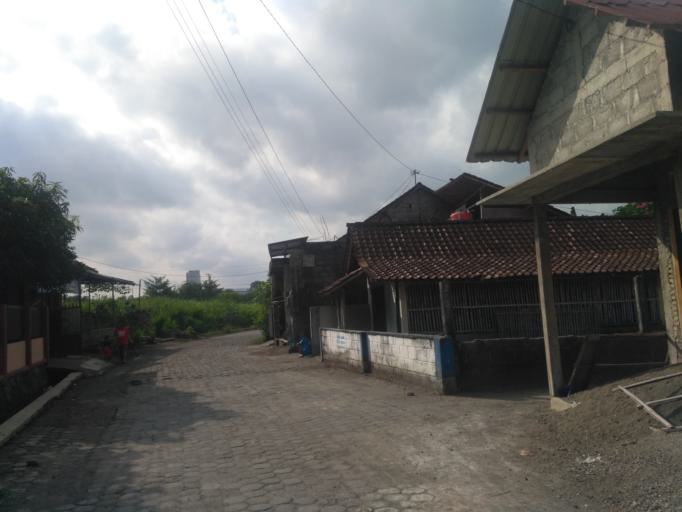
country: ID
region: Daerah Istimewa Yogyakarta
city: Melati
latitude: -7.7533
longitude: 110.3497
